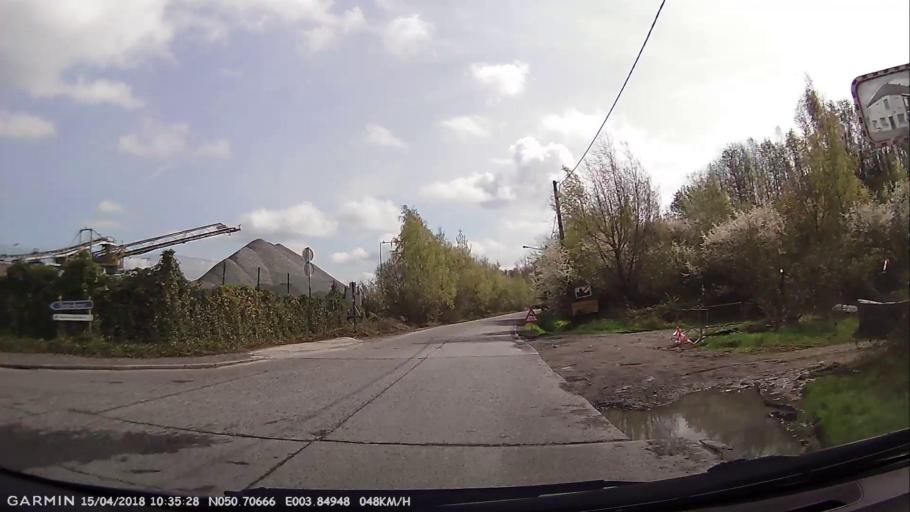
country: BE
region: Wallonia
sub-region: Province du Hainaut
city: Lessines
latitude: 50.7067
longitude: 3.8496
